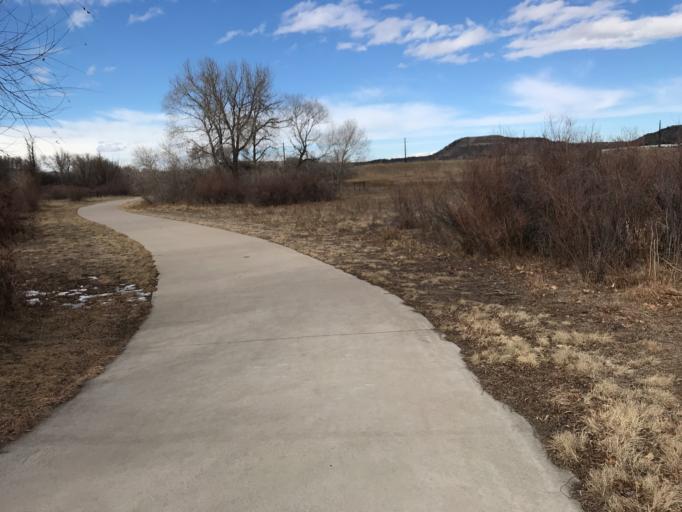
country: US
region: Colorado
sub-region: Douglas County
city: Castle Rock
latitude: 39.3944
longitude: -104.8699
